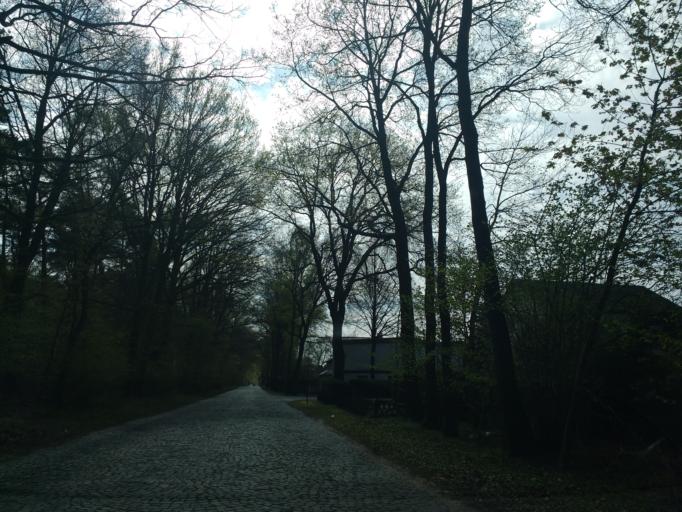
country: DE
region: North Rhine-Westphalia
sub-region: Regierungsbezirk Detmold
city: Paderborn
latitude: 51.7821
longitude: 8.7197
